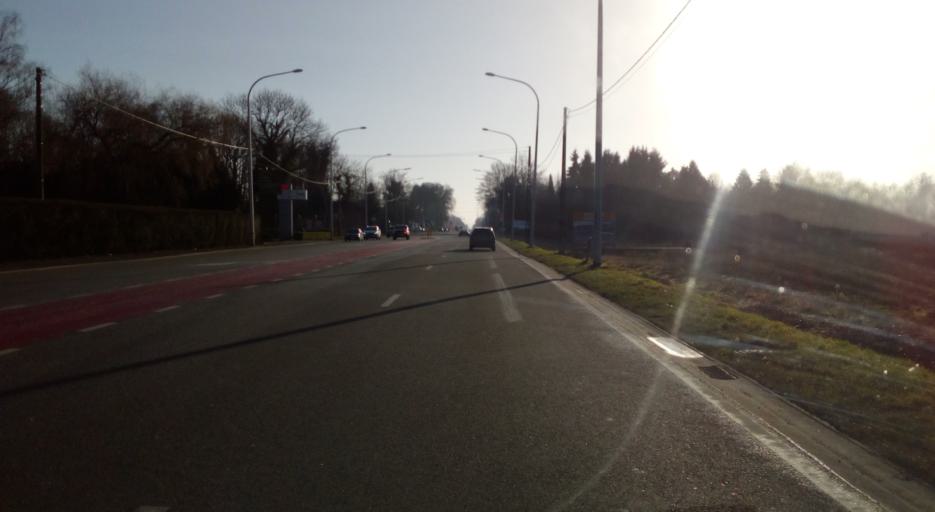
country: BE
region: Wallonia
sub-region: Province du Hainaut
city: Gerpinnes
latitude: 50.3364
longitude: 4.4745
